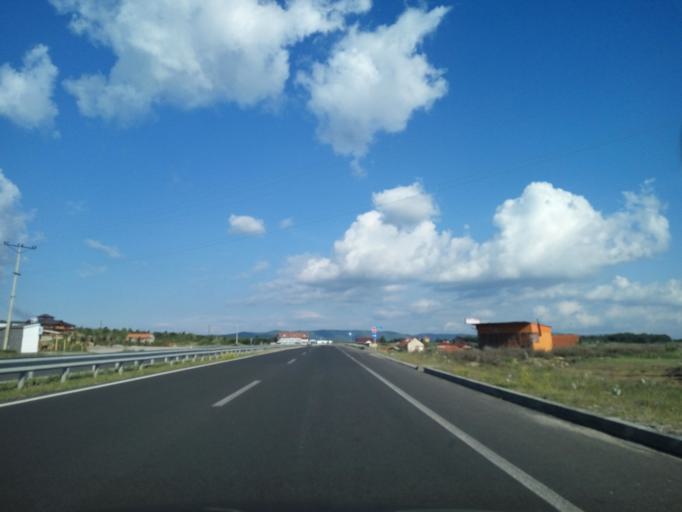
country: XK
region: Prizren
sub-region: Komuna e Malisheves
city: Llazice
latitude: 42.5657
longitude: 20.7622
